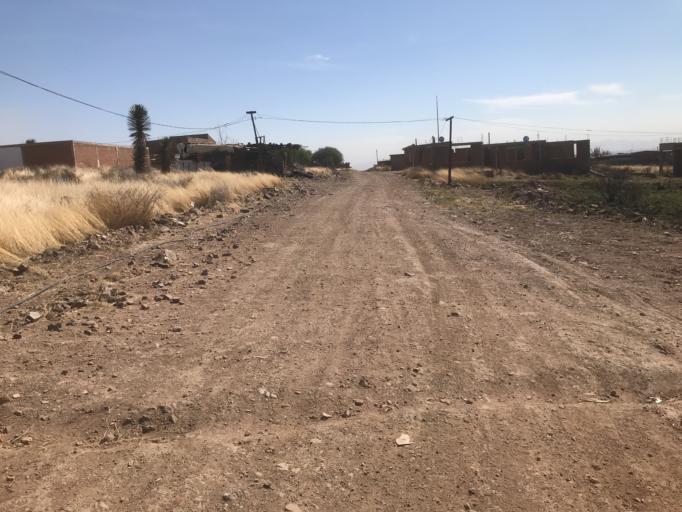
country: MX
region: Durango
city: Victoria de Durango
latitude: 24.0349
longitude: -104.7131
